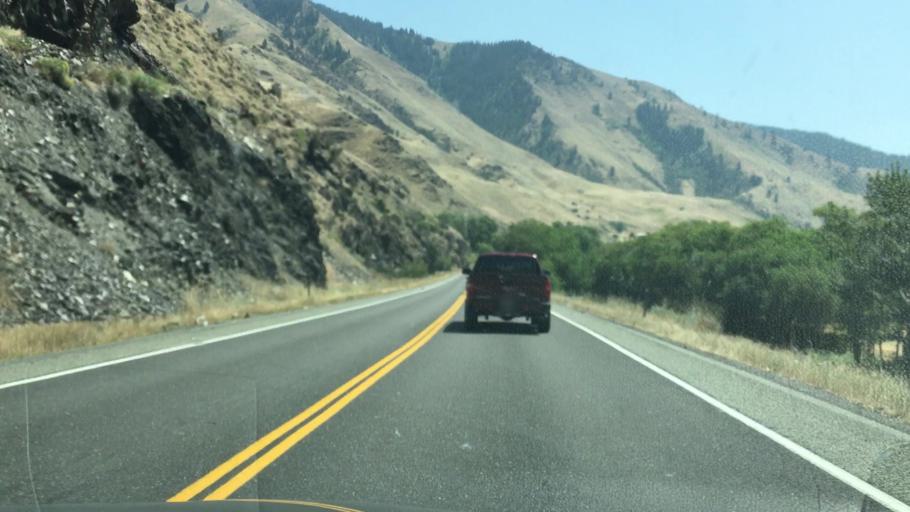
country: US
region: Idaho
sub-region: Valley County
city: McCall
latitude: 45.3464
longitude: -116.3539
